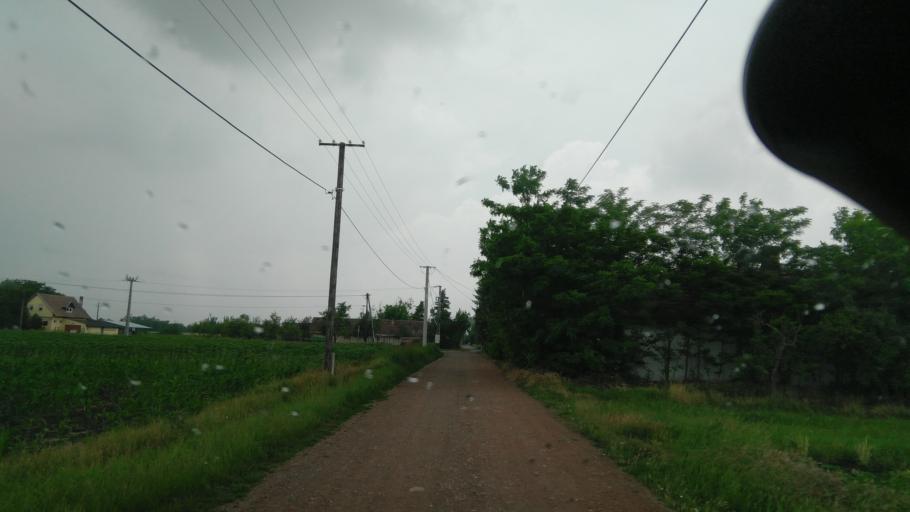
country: HU
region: Bekes
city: Bekescsaba
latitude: 46.7013
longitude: 21.1257
